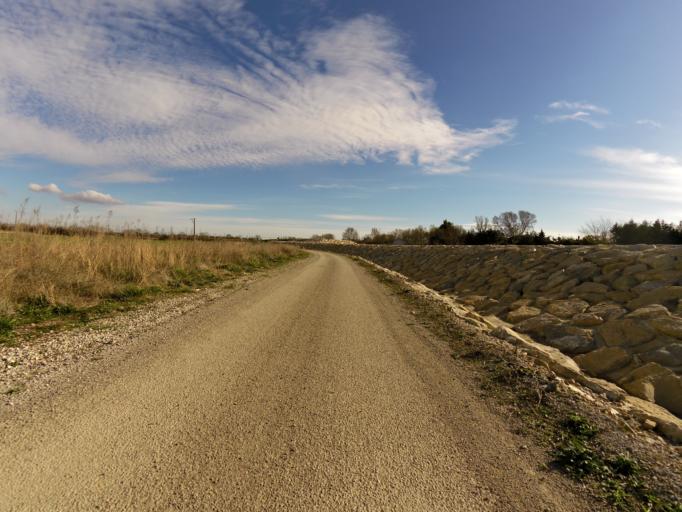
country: FR
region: Languedoc-Roussillon
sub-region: Departement du Gard
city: Gallargues-le-Montueux
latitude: 43.7147
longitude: 4.1565
